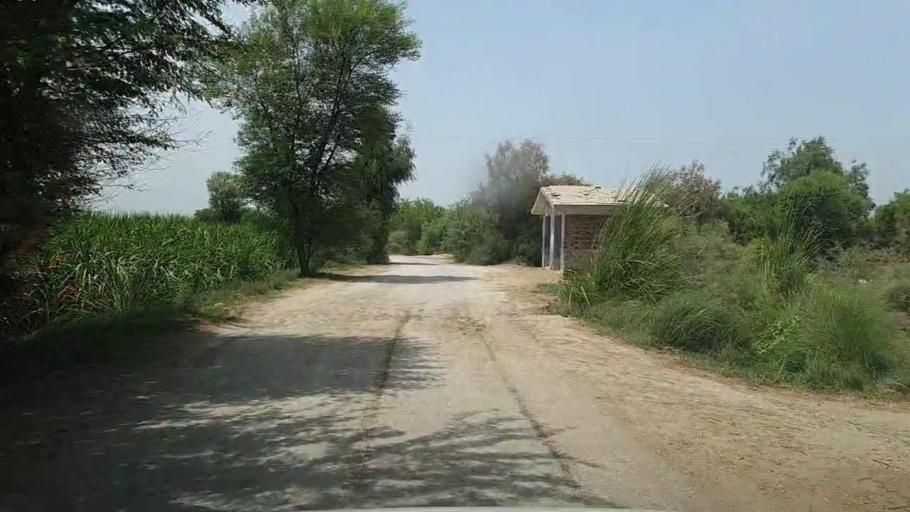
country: PK
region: Sindh
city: Pano Aqil
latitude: 27.8163
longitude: 69.2388
